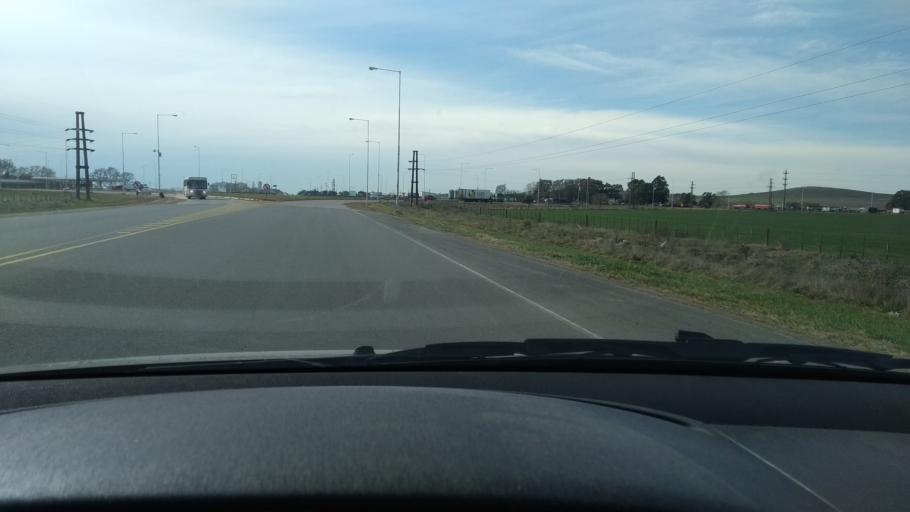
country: AR
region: Buenos Aires
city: Olavarria
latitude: -36.9386
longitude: -60.2323
